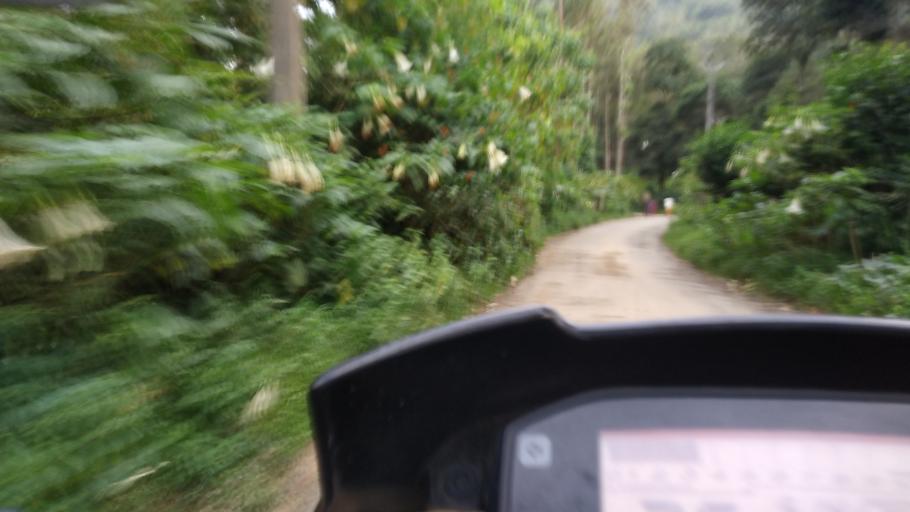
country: IN
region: Tamil Nadu
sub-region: Theni
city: Bodinayakkanur
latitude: 10.0242
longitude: 77.2473
